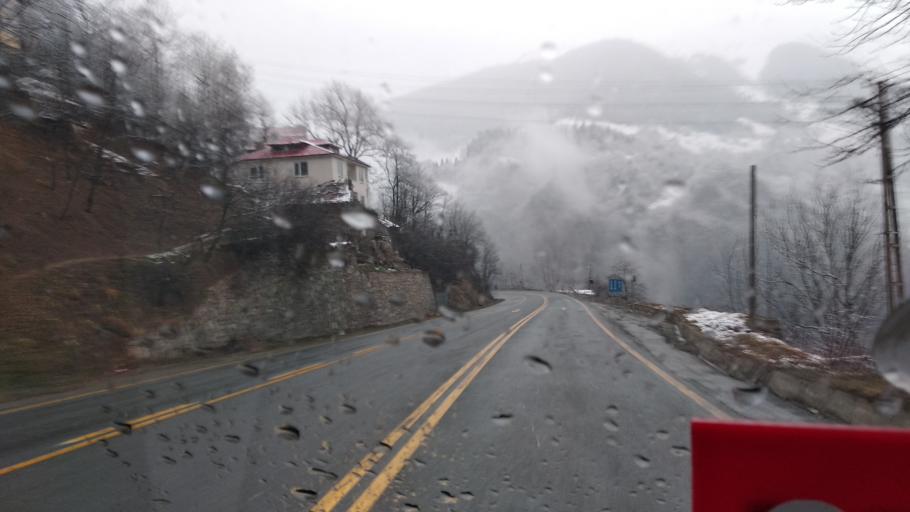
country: TR
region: Gumushane
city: Yaglidere
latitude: 40.6993
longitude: 39.4819
